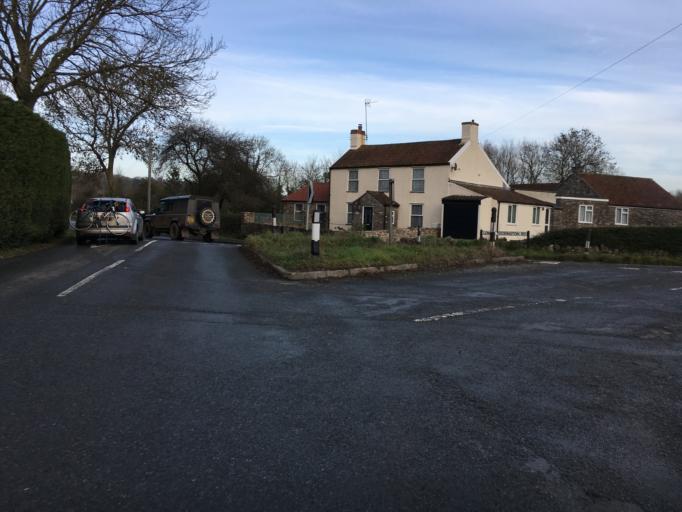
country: GB
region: England
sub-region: South Gloucestershire
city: Almondsbury
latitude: 51.5698
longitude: -2.5681
